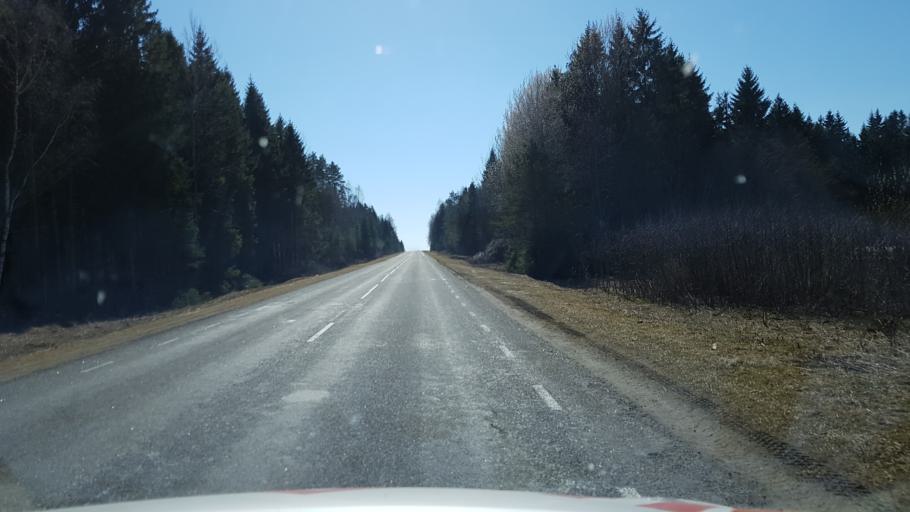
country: EE
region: Laeaene-Virumaa
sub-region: Tamsalu vald
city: Tamsalu
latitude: 59.1291
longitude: 26.0379
